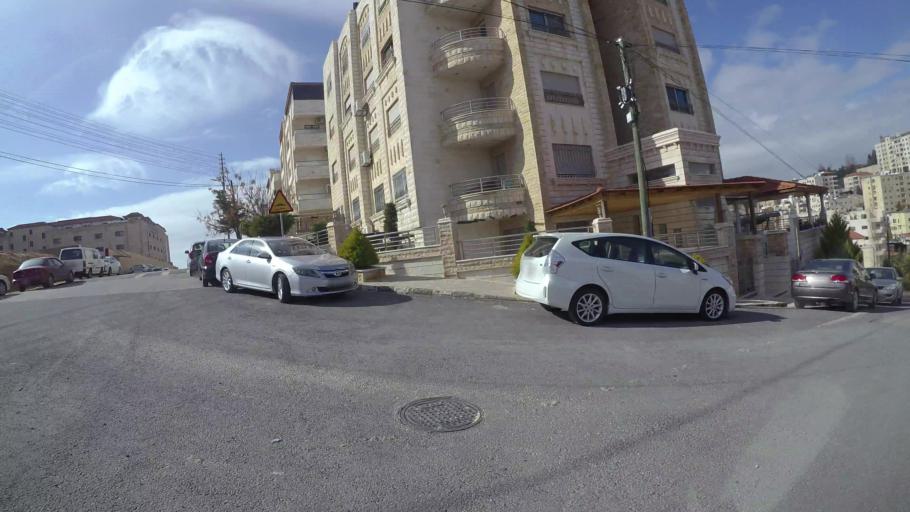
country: JO
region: Amman
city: Al Jubayhah
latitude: 32.0057
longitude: 35.8487
